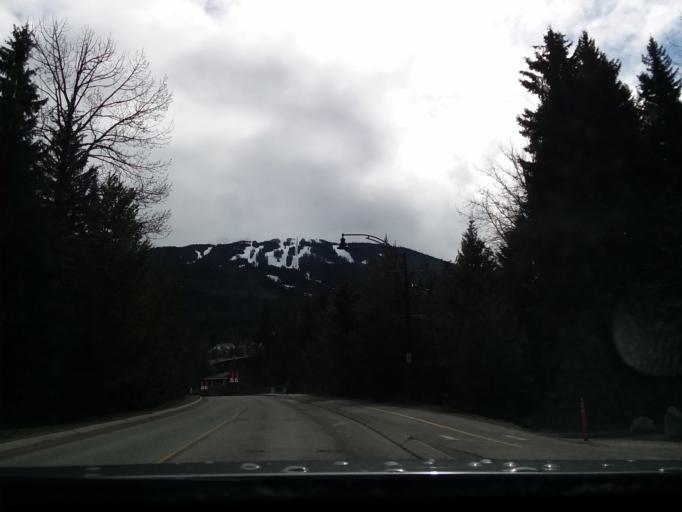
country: CA
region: British Columbia
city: Whistler
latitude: 50.1199
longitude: -122.9500
